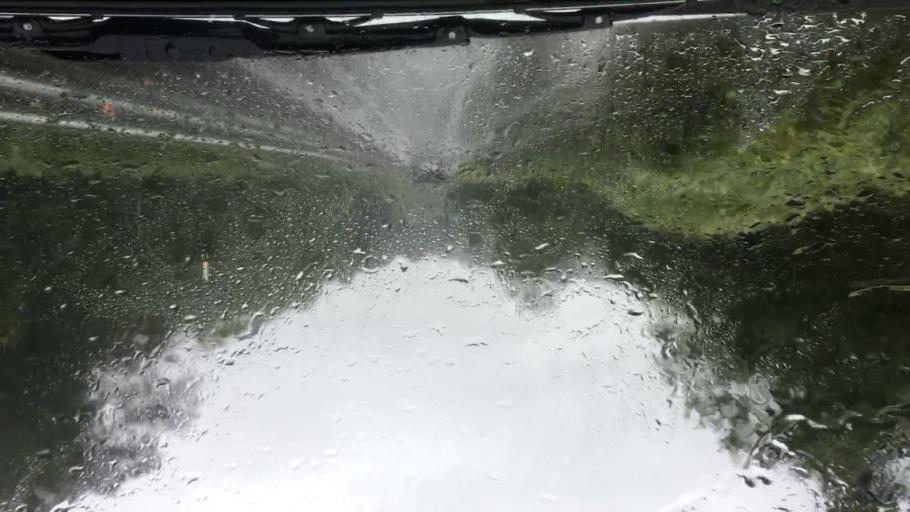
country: JP
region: Hokkaido
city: Otaru
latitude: 42.8487
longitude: 141.0473
